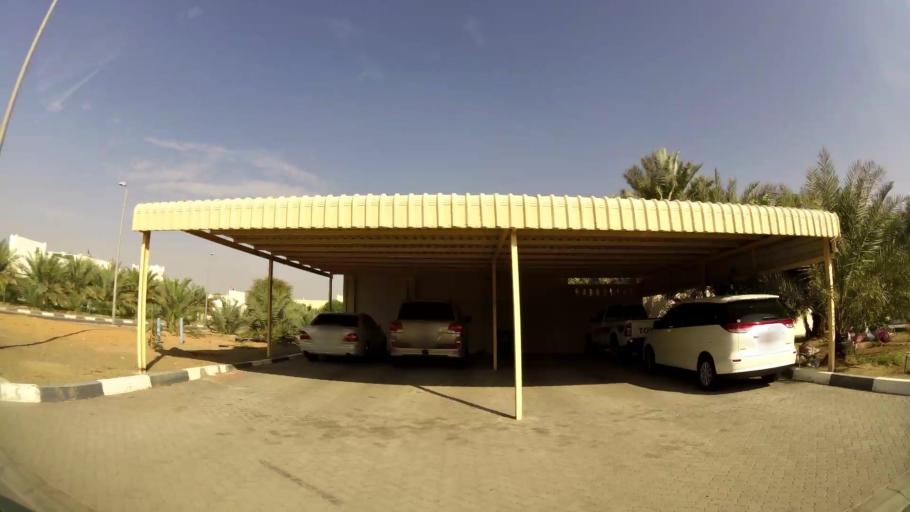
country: AE
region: Abu Dhabi
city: Al Ain
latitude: 24.0747
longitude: 55.8686
